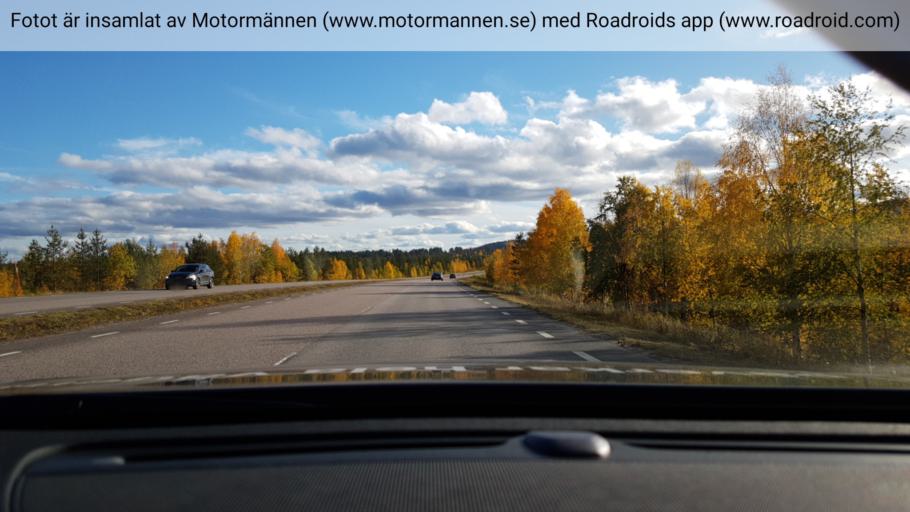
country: SE
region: Norrbotten
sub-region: Gallivare Kommun
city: Malmberget
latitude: 67.1559
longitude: 20.6615
